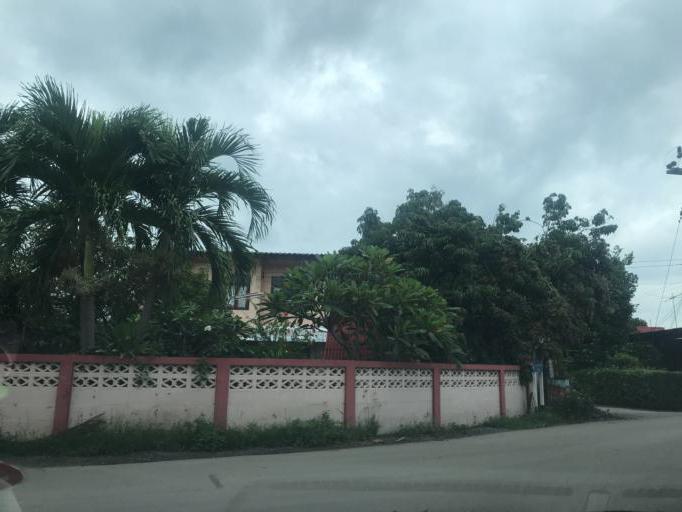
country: TH
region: Chiang Mai
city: Saraphi
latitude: 18.6956
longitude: 99.0216
